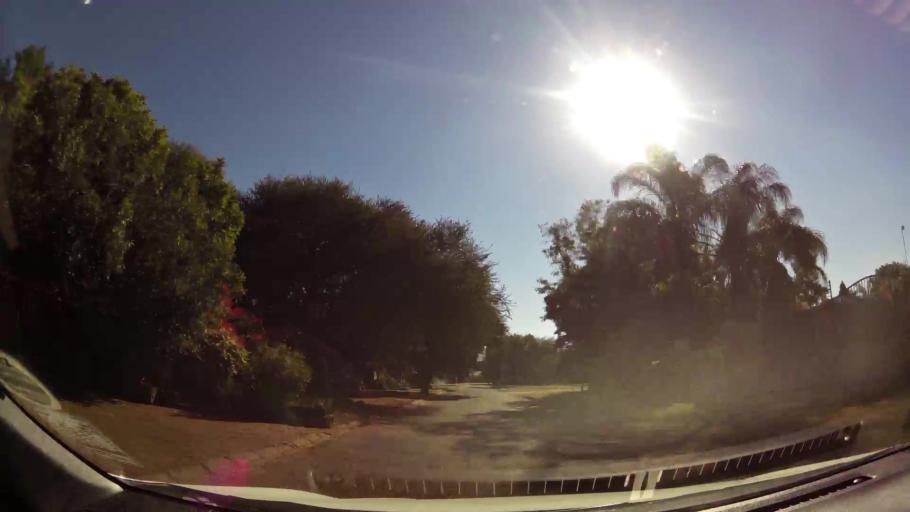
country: ZA
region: Limpopo
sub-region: Waterberg District Municipality
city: Mokopane
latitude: -24.2110
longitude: 28.9952
